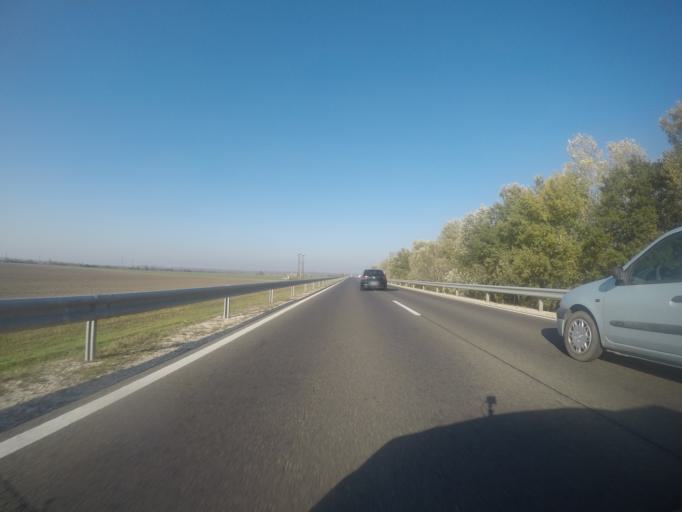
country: HU
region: Fejer
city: Ercsi
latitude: 47.2122
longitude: 18.8845
